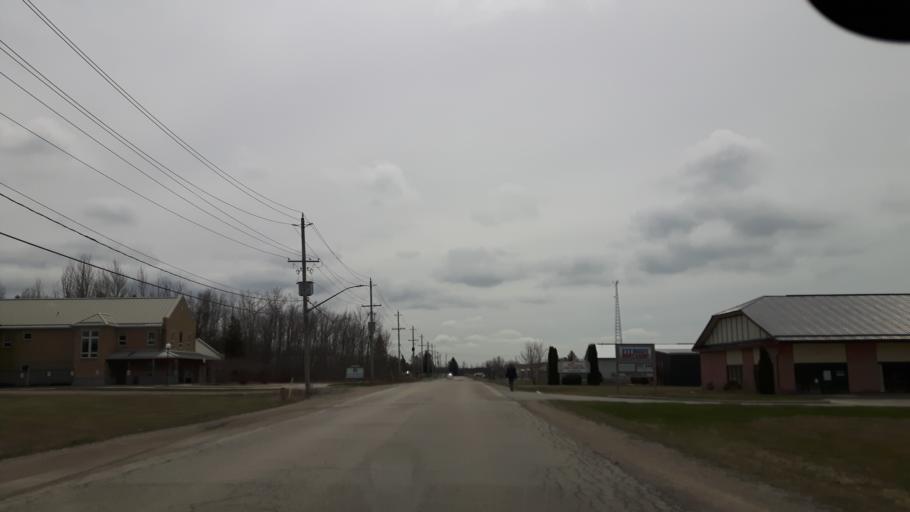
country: CA
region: Ontario
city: Goderich
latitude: 43.7308
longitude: -81.6995
